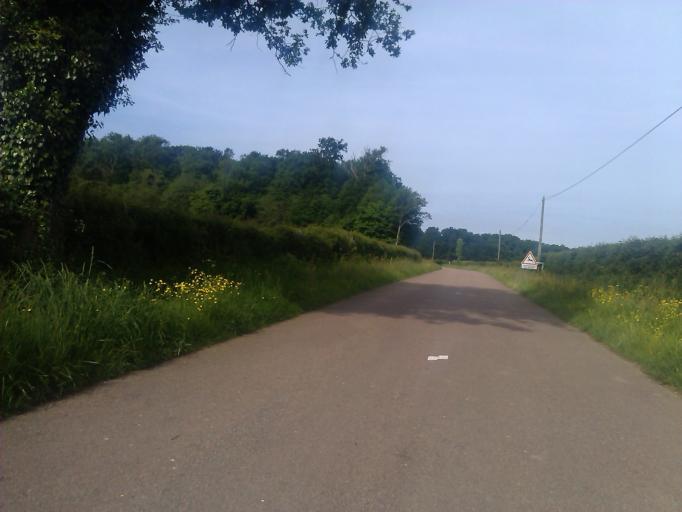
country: FR
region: Auvergne
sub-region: Departement de l'Allier
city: Cerilly
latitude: 46.6156
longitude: 2.7421
